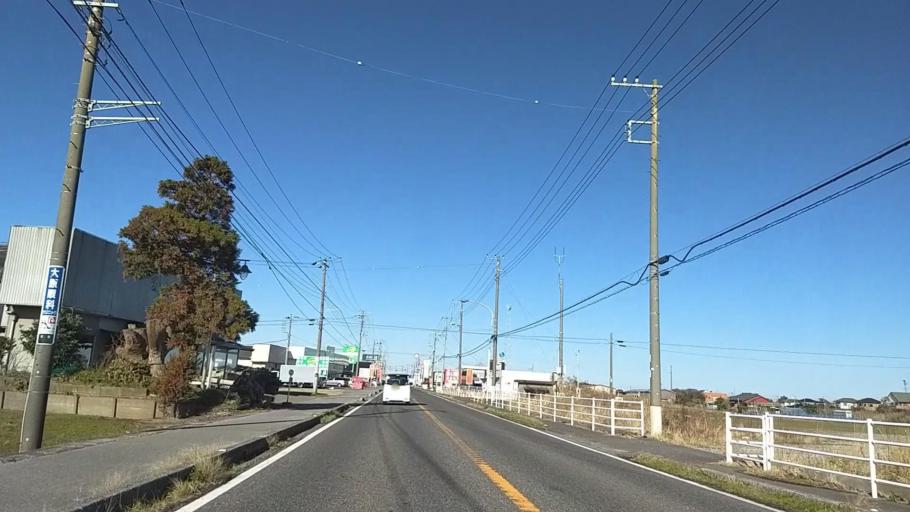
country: JP
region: Chiba
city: Ohara
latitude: 35.2723
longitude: 140.3941
